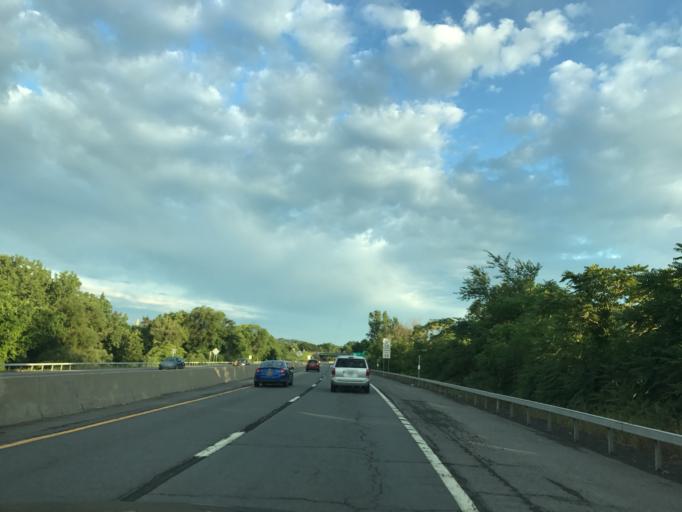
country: US
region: New York
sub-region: Albany County
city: Green Island
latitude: 42.7488
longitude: -73.6991
